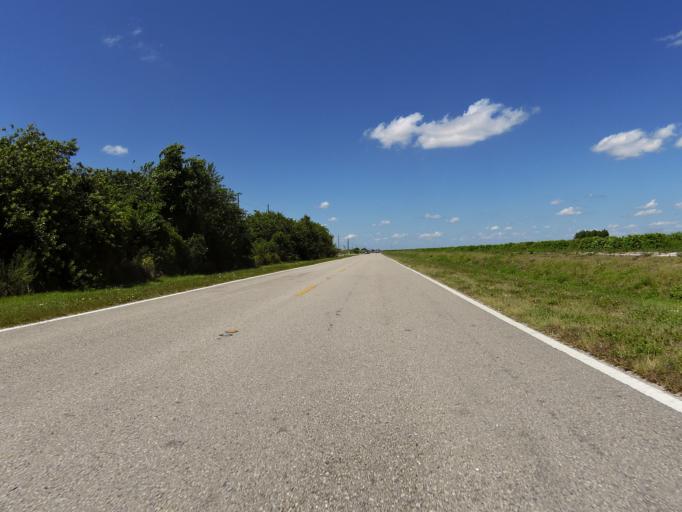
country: US
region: Florida
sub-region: Collier County
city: Immokalee
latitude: 26.3069
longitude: -81.4161
